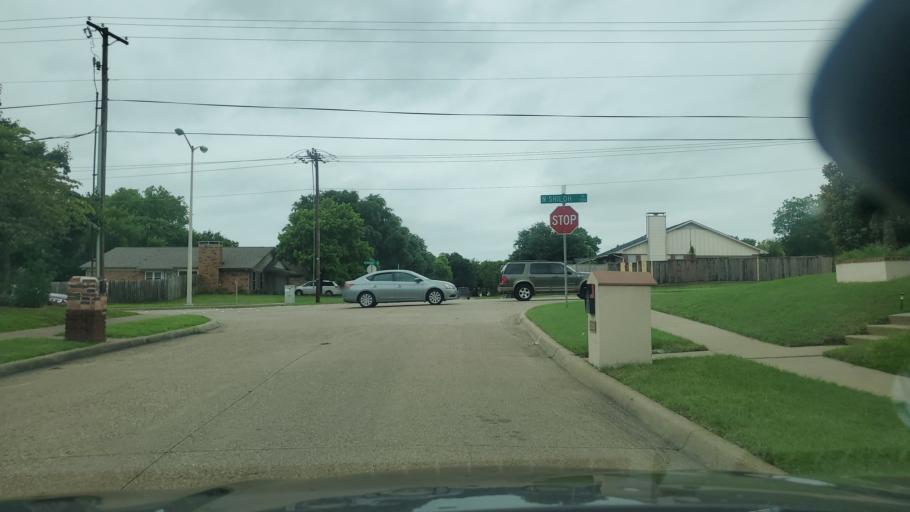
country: US
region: Texas
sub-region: Dallas County
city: Garland
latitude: 32.9528
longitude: -96.6649
